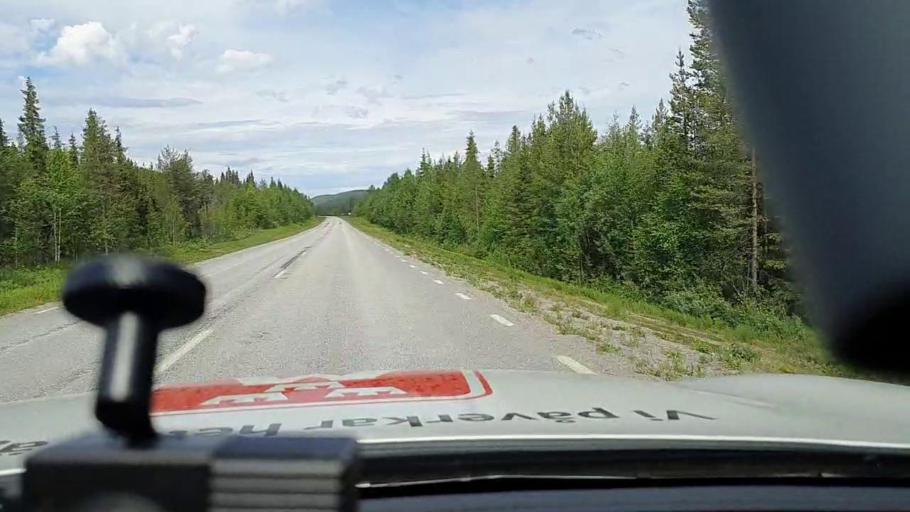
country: SE
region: Norrbotten
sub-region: Jokkmokks Kommun
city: Jokkmokk
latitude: 66.5489
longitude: 20.1257
